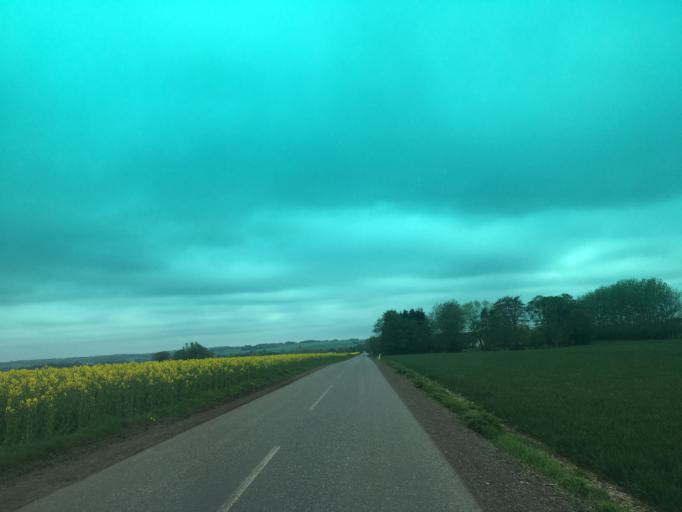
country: DK
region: Zealand
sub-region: Ringsted Kommune
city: Ringsted
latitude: 55.4264
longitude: 11.7122
